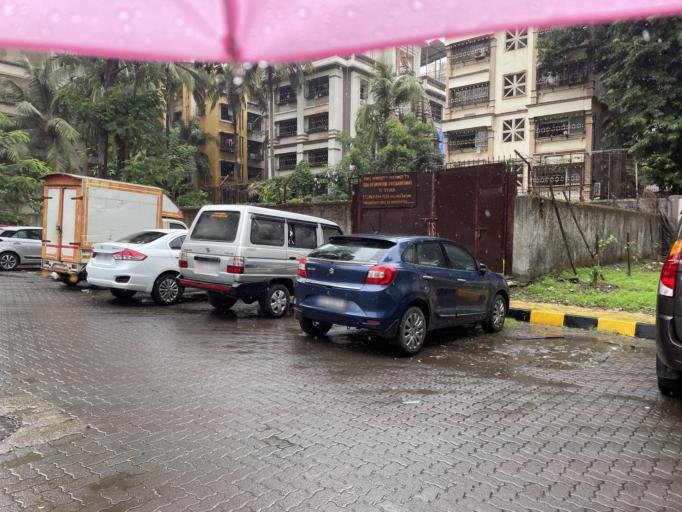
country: IN
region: Maharashtra
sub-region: Mumbai Suburban
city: Borivli
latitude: 19.2355
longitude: 72.8615
